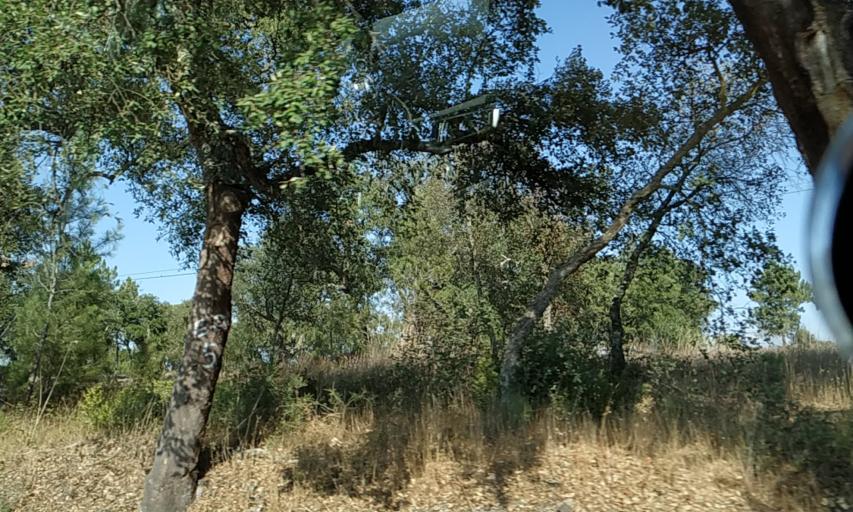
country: PT
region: Santarem
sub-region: Benavente
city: Poceirao
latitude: 38.7574
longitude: -8.6325
